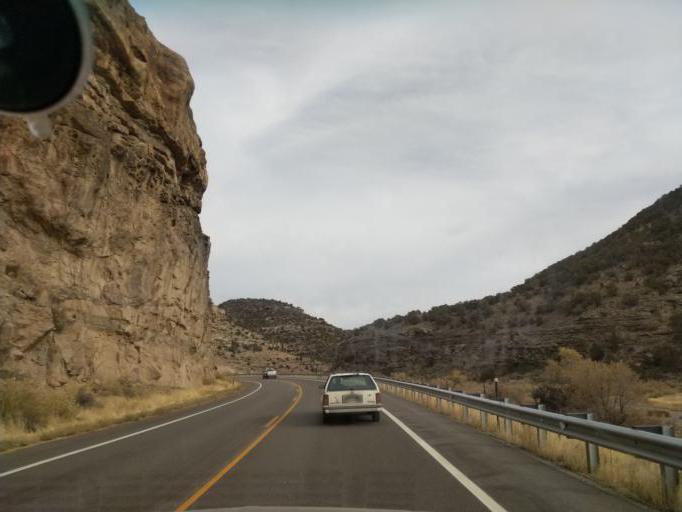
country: US
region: Colorado
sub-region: Mesa County
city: Palisade
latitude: 39.1957
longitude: -108.2240
